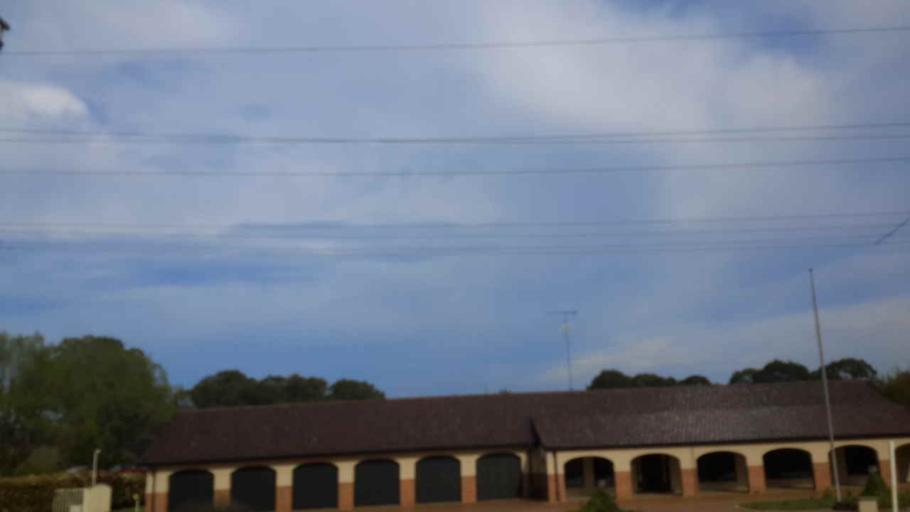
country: AU
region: New South Wales
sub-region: Penrith Municipality
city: Glenmore Park
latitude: -33.7949
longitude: 150.6987
